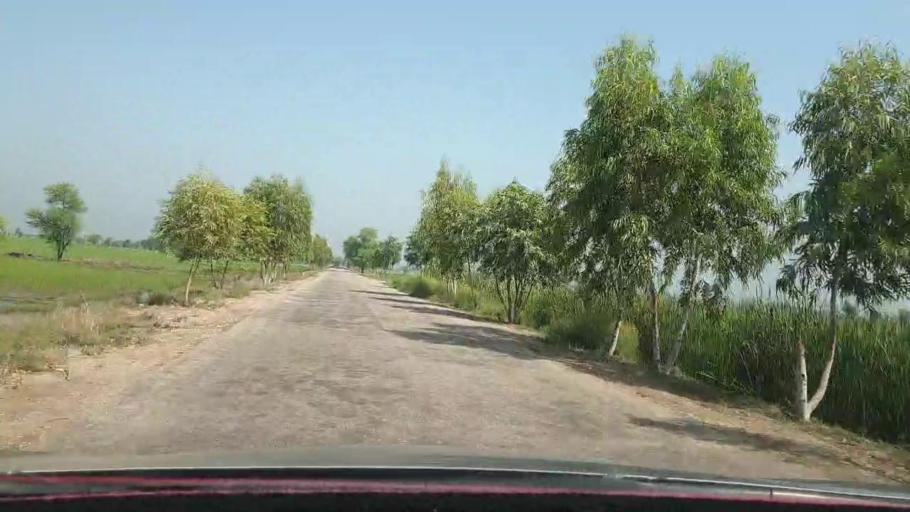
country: PK
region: Sindh
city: Warah
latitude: 27.4689
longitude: 67.8335
